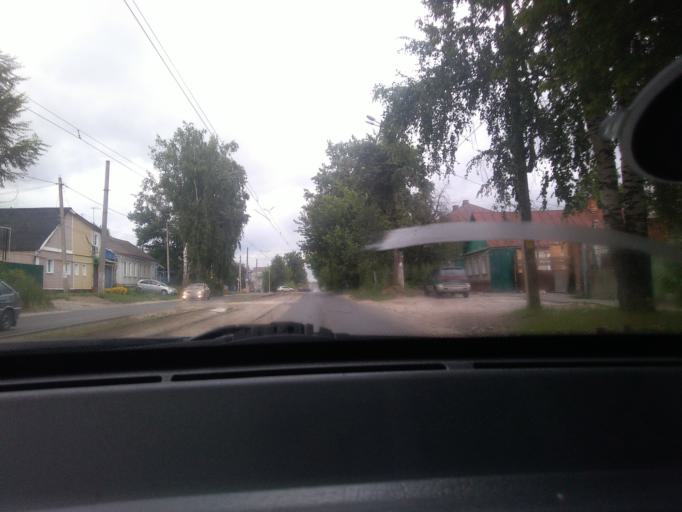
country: RU
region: Kursk
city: Kursk
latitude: 51.7362
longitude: 36.1762
